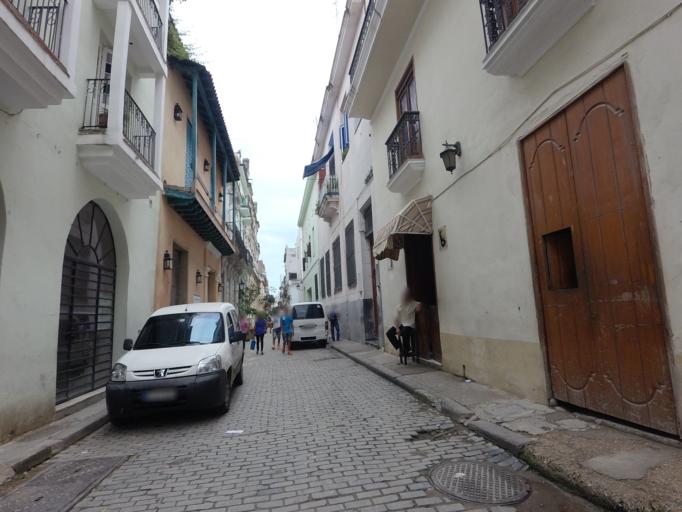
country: CU
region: La Habana
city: La Habana Vieja
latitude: 23.1366
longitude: -82.3507
